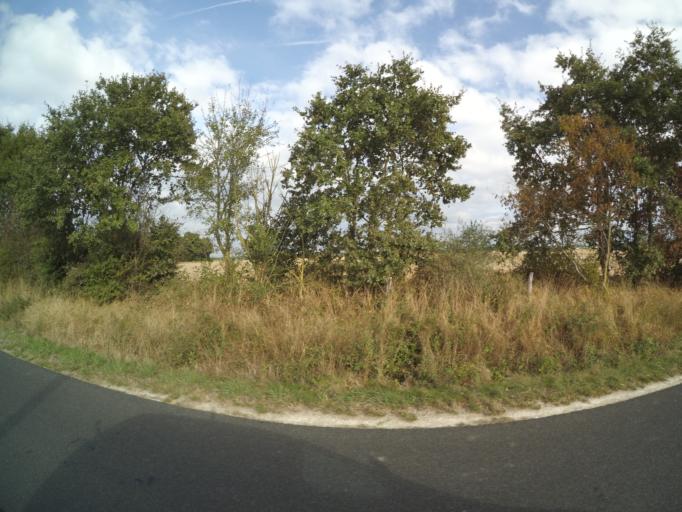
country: FR
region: Centre
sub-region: Departement d'Indre-et-Loire
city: Nazelles-Negron
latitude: 47.4786
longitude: 0.9515
